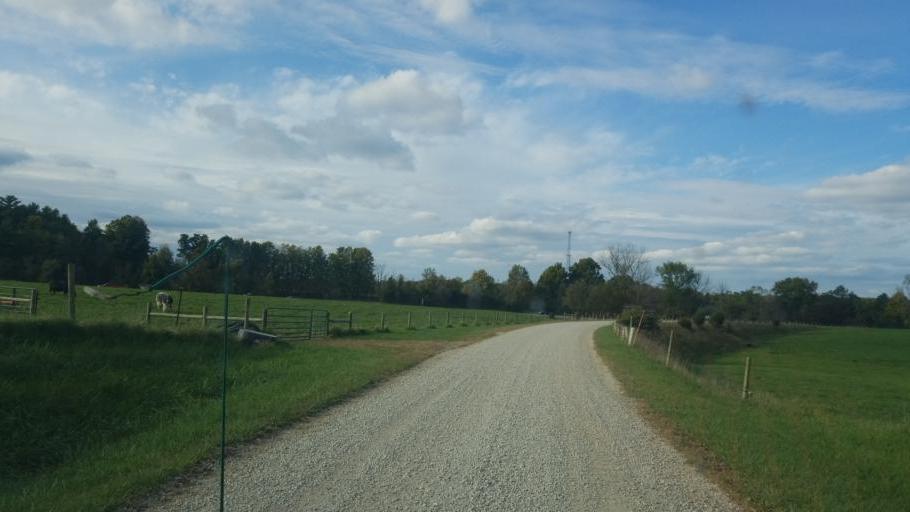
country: US
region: Ohio
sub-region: Morrow County
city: Mount Gilead
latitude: 40.5154
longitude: -82.6875
